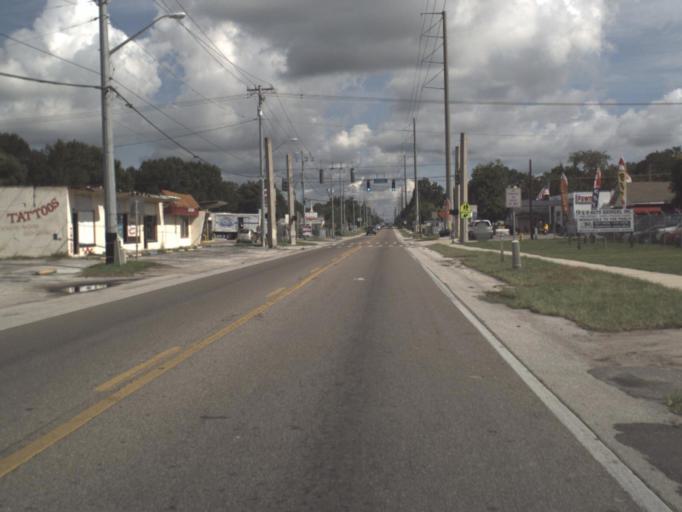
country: US
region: Florida
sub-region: Polk County
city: Combee Settlement
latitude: 28.0544
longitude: -81.9080
